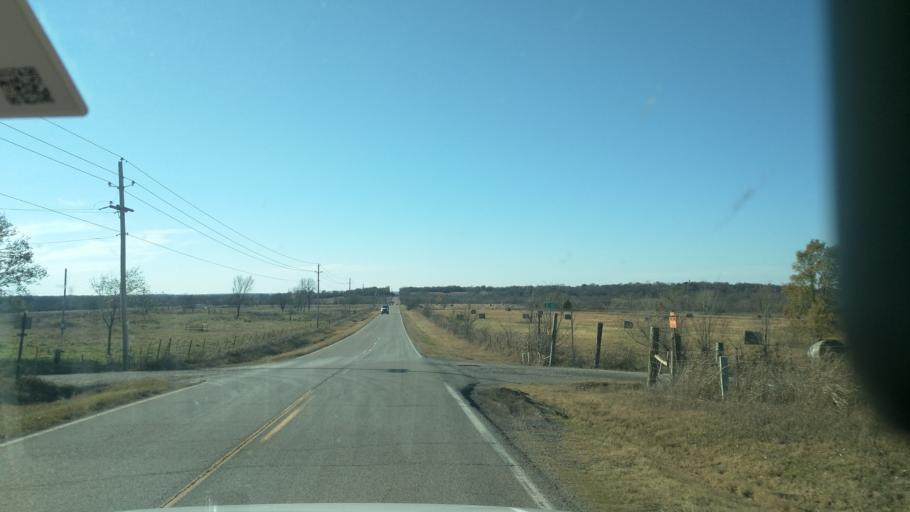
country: US
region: Oklahoma
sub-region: Nowata County
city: Nowata
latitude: 36.7717
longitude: -95.5570
